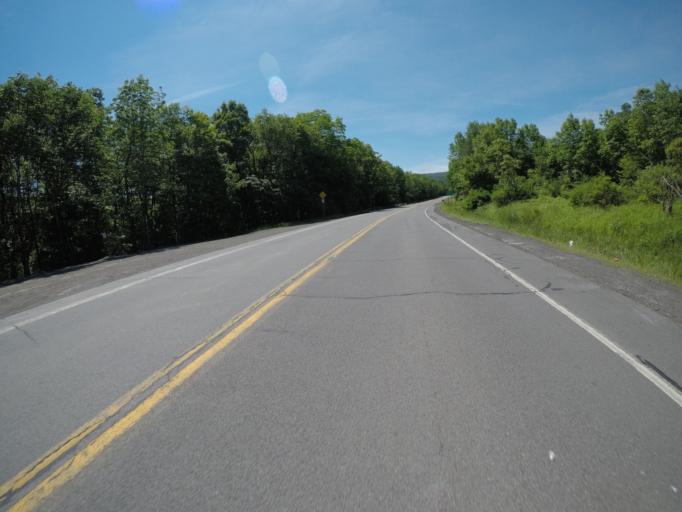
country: US
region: New York
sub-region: Delaware County
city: Delhi
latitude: 42.2206
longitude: -74.9677
